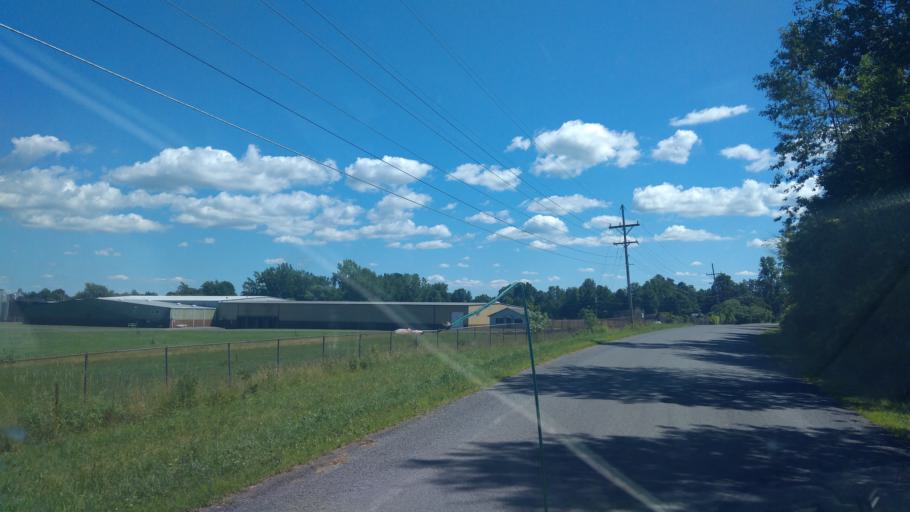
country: US
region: New York
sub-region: Wayne County
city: Sodus
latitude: 43.2085
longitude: -77.0242
